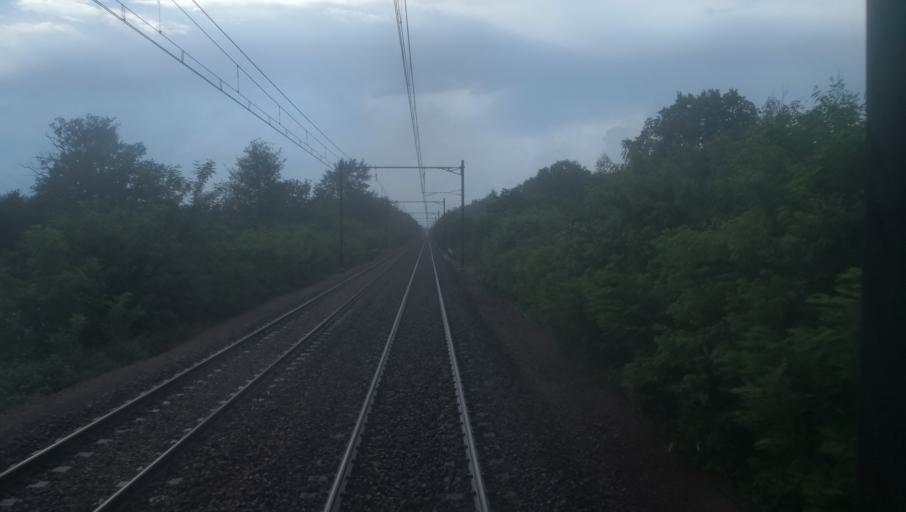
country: FR
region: Centre
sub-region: Departement du Loiret
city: La Ferte-Saint-Aubin
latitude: 47.6701
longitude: 1.9641
